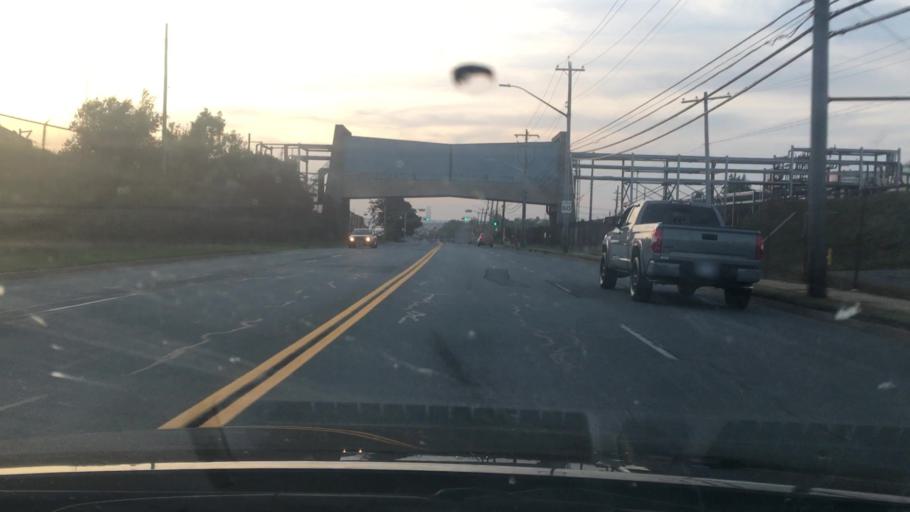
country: CA
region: Nova Scotia
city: Halifax
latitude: 44.6404
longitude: -63.5328
